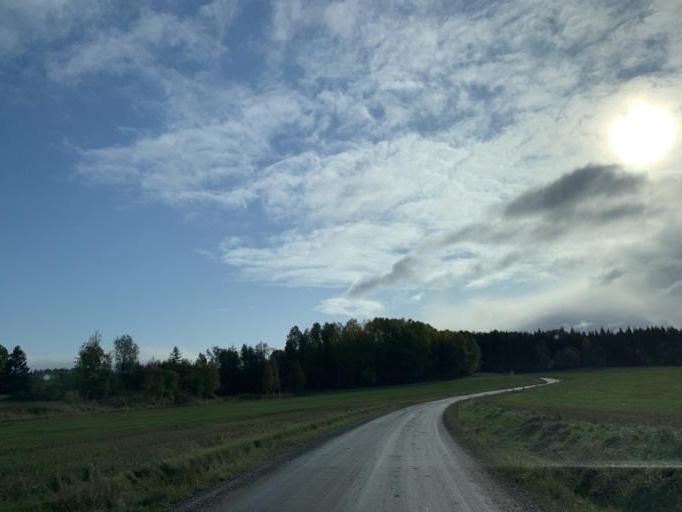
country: SE
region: Soedermanland
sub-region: Eskilstuna Kommun
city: Kvicksund
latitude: 59.3980
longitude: 16.2377
